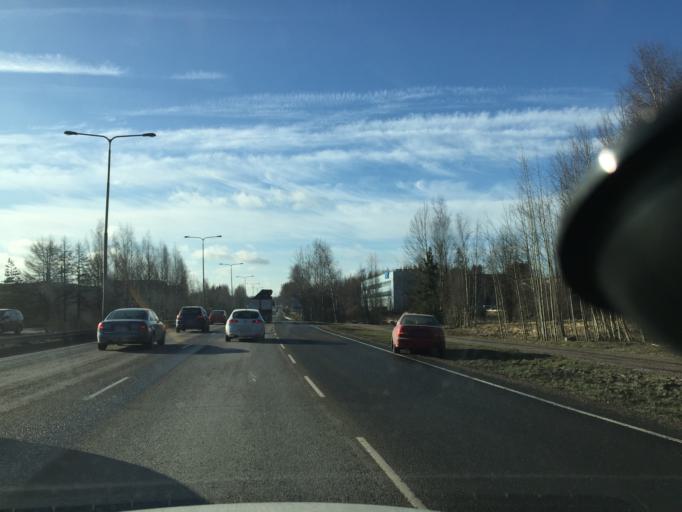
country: FI
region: Uusimaa
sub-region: Helsinki
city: Teekkarikylae
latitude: 60.2708
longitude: 24.8745
